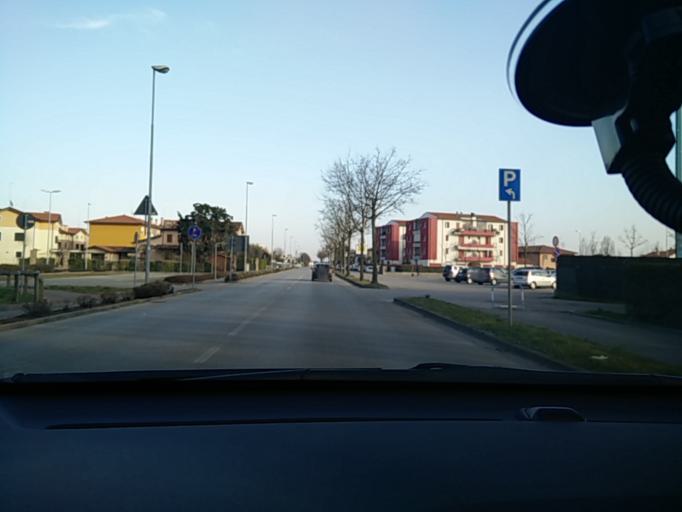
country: IT
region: Veneto
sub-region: Provincia di Venezia
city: San Dona di Piave
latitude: 45.6240
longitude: 12.5849
